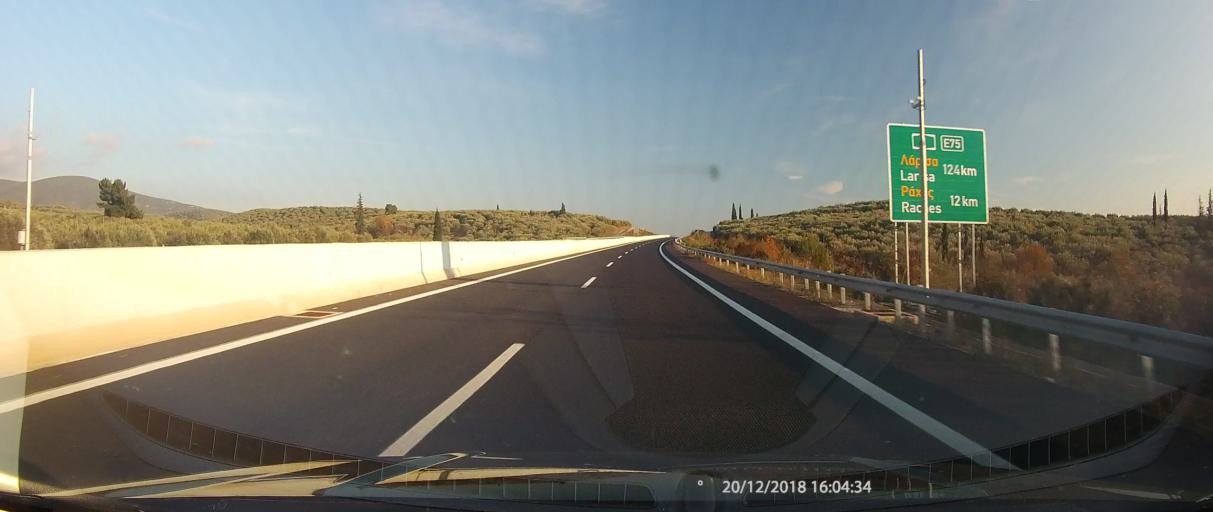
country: GR
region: Central Greece
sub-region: Nomos Fthiotidos
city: Stylida
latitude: 38.9111
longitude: 22.6655
